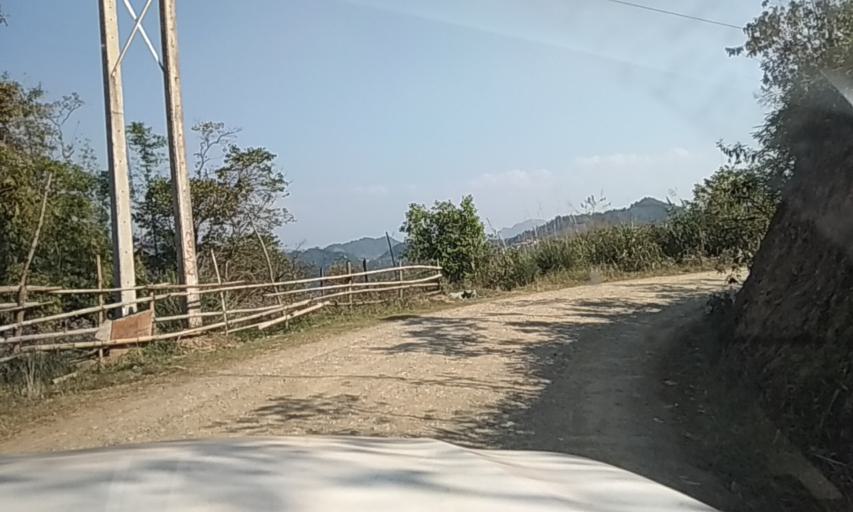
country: LA
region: Phongsali
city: Phongsali
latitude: 21.6572
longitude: 102.0910
